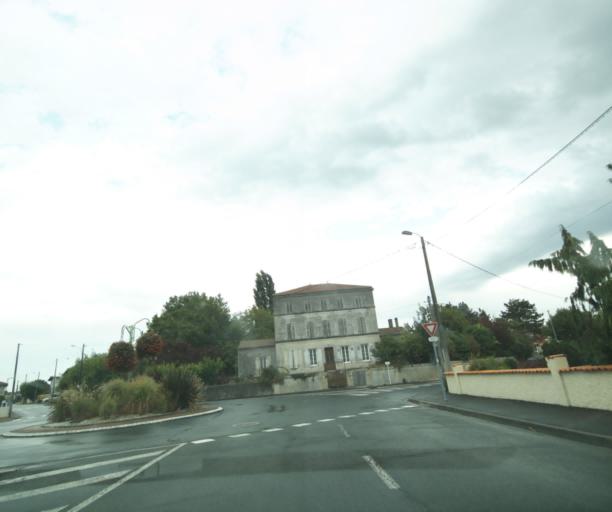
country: FR
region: Poitou-Charentes
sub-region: Departement de la Charente-Maritime
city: Tonnay-Charente
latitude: 45.9451
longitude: -0.8907
